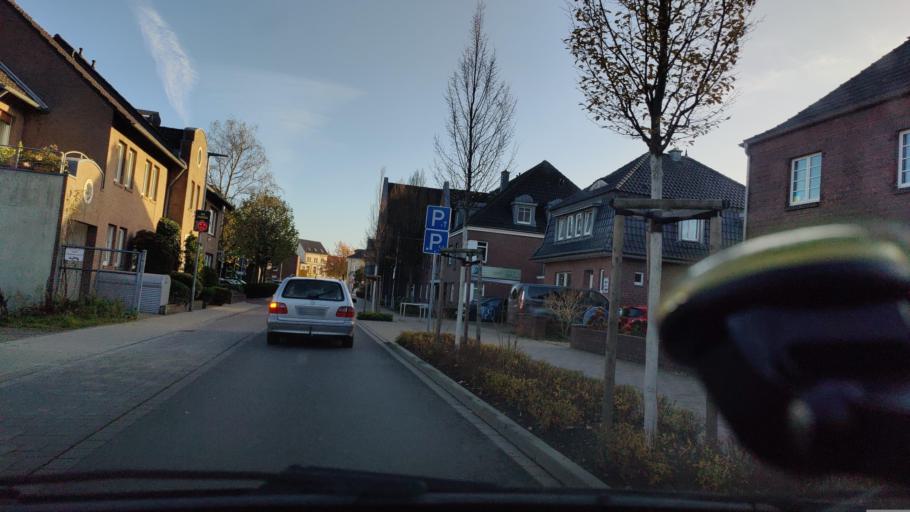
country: DE
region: North Rhine-Westphalia
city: Straelen
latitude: 51.4443
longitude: 6.2645
